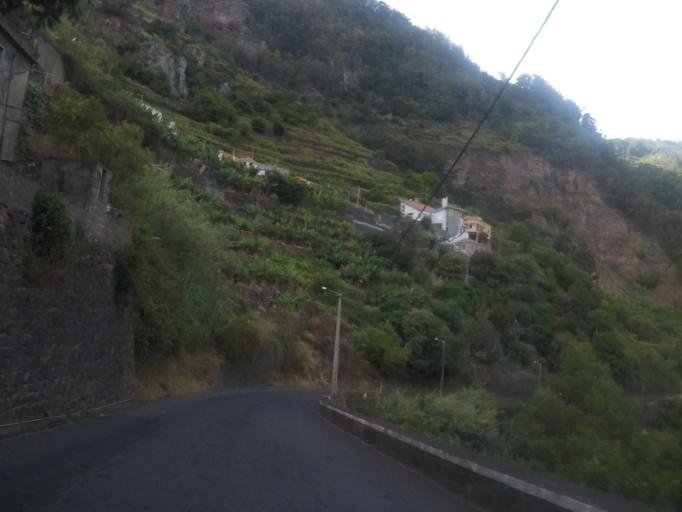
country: PT
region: Madeira
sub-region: Calheta
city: Arco da Calheta
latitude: 32.7130
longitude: -17.1348
